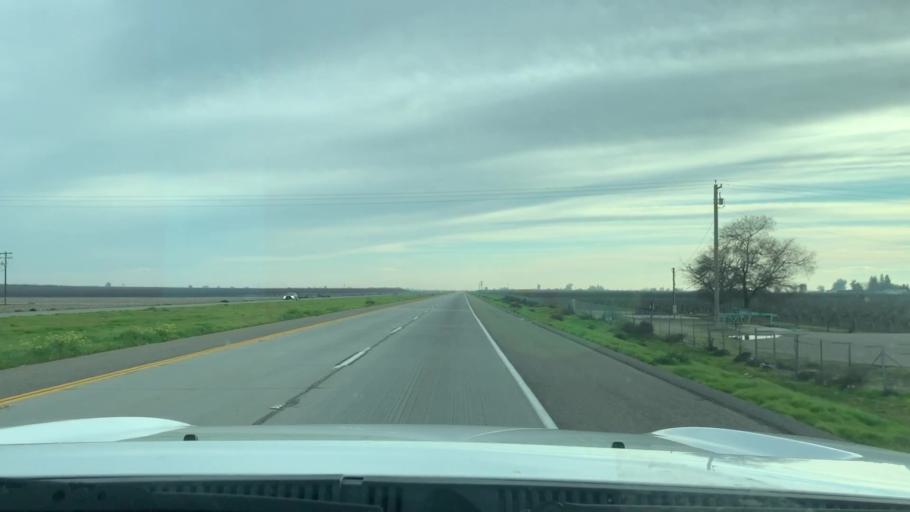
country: US
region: California
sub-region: Fresno County
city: Easton
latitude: 36.5912
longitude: -119.7862
